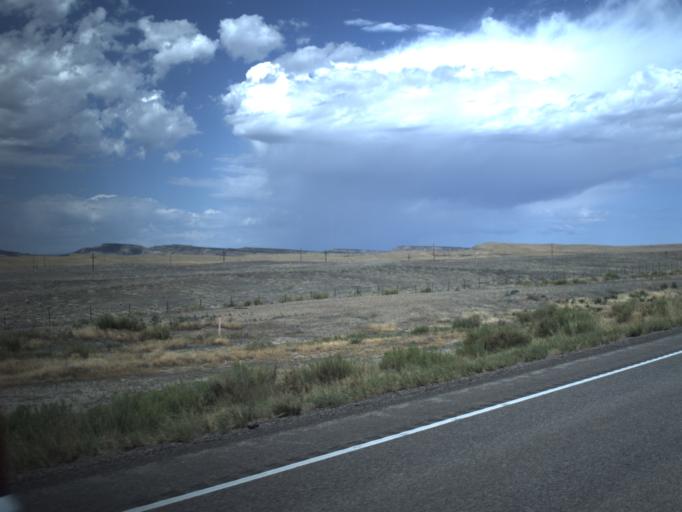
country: US
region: Utah
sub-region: Carbon County
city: East Carbon City
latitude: 39.3622
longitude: -110.3900
